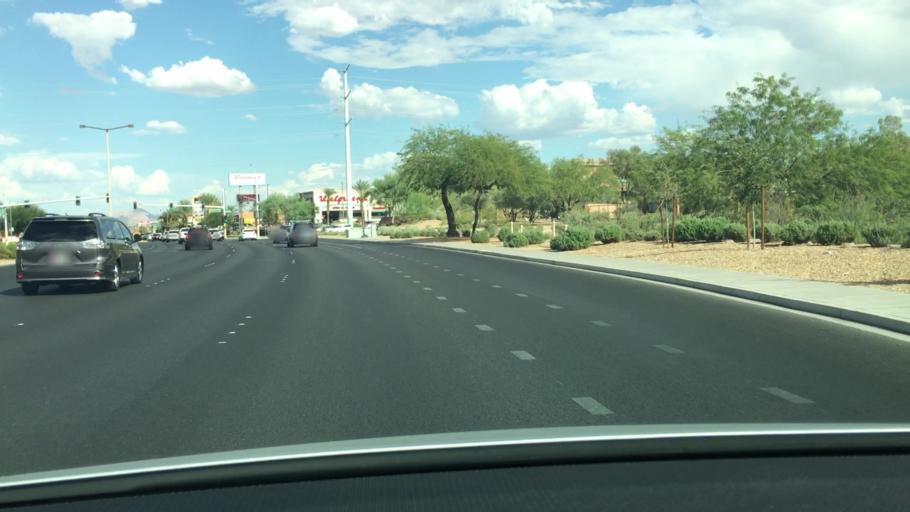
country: US
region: Nevada
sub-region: Clark County
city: Spring Valley
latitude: 36.1962
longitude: -115.2621
